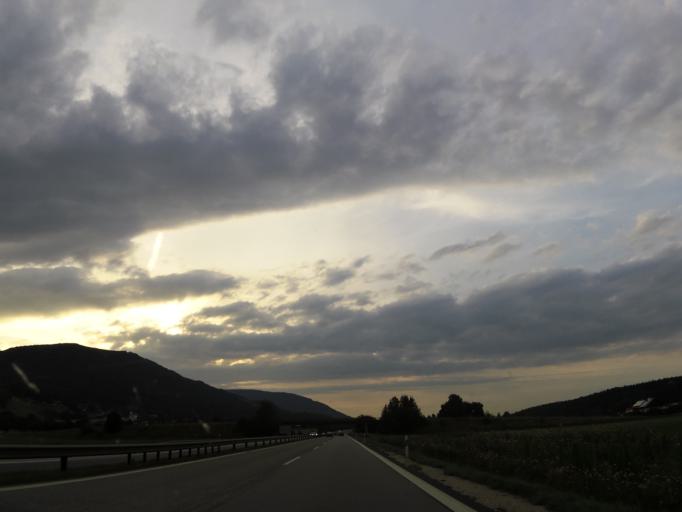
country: DE
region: Bavaria
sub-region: Upper Bavaria
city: Piding
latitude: 47.7771
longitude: 12.8837
